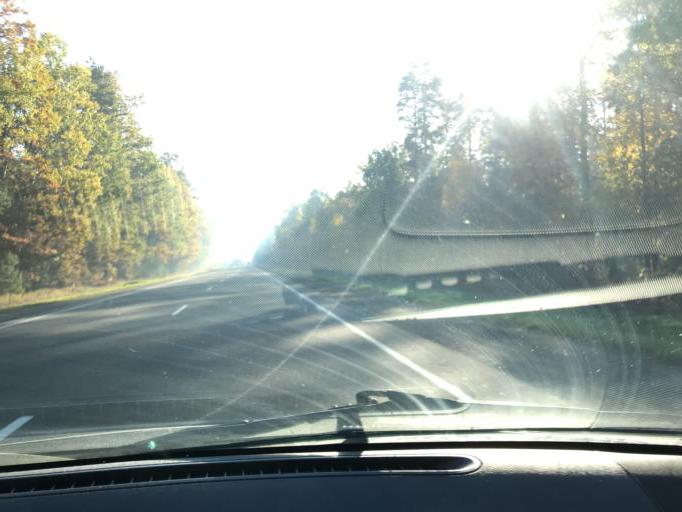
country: BY
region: Brest
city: Horad Luninyets
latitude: 52.2889
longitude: 26.7834
